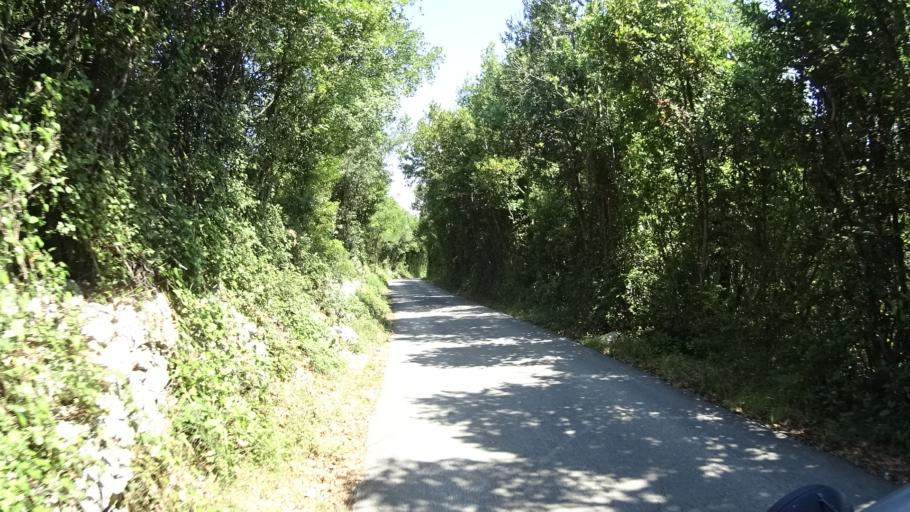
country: HR
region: Istarska
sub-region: Grad Labin
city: Rabac
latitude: 44.9938
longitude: 14.1646
